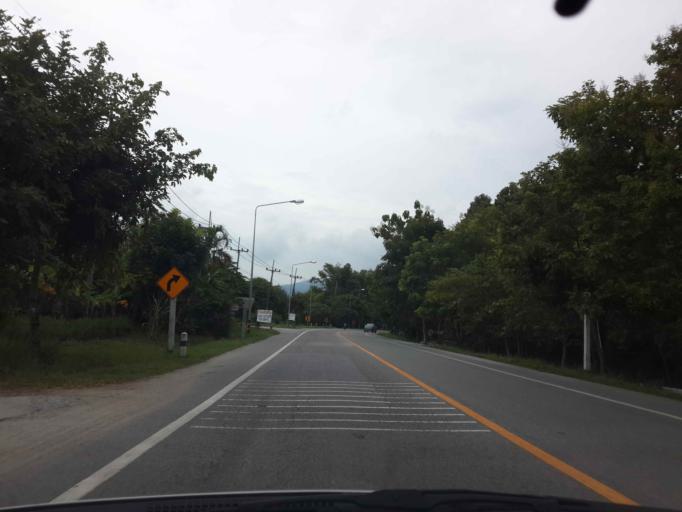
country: TH
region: Chon Buri
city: Si Racha
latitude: 13.2331
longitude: 100.9901
